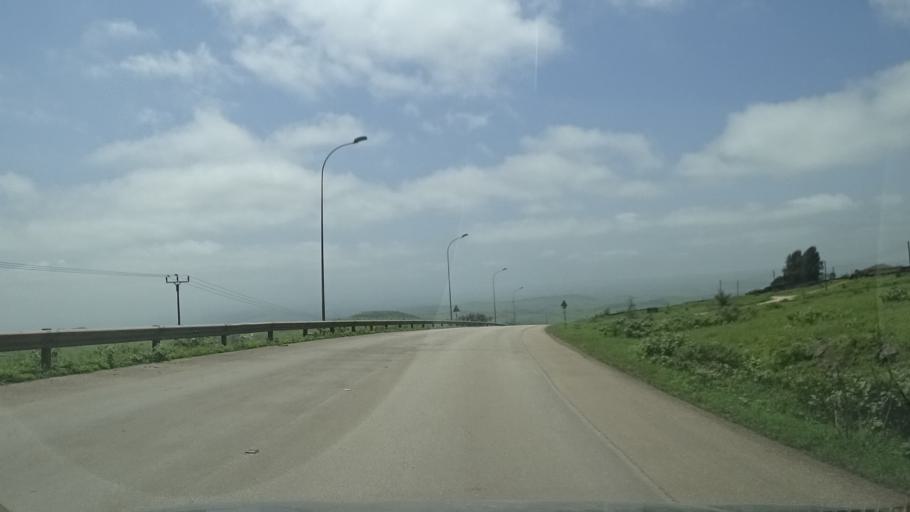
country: OM
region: Zufar
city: Salalah
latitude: 17.1753
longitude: 54.2432
